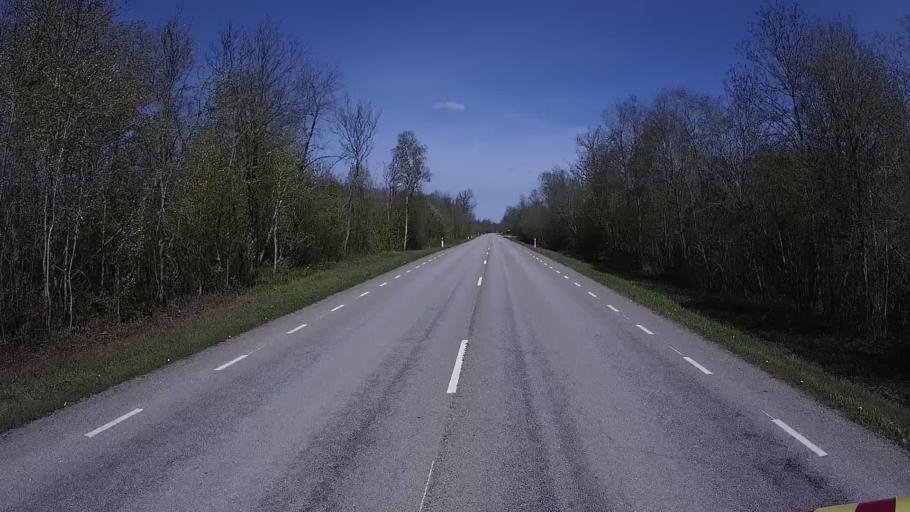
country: EE
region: Laeaene
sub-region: Ridala Parish
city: Uuemoisa
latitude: 58.9691
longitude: 23.6768
